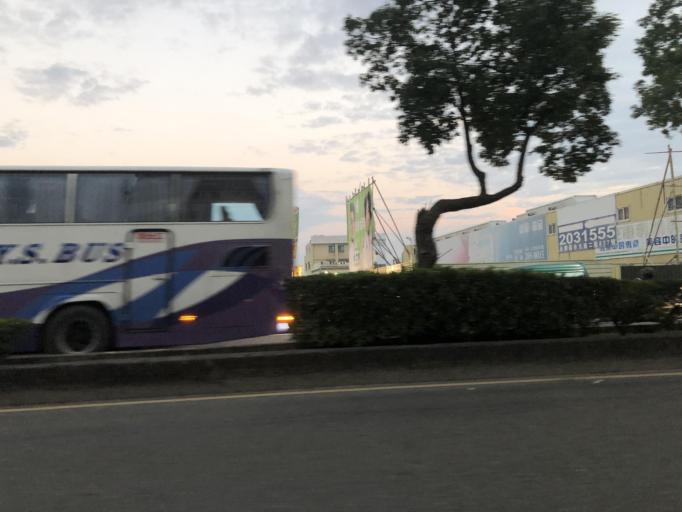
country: TW
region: Taiwan
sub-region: Tainan
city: Tainan
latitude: 23.0188
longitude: 120.2623
